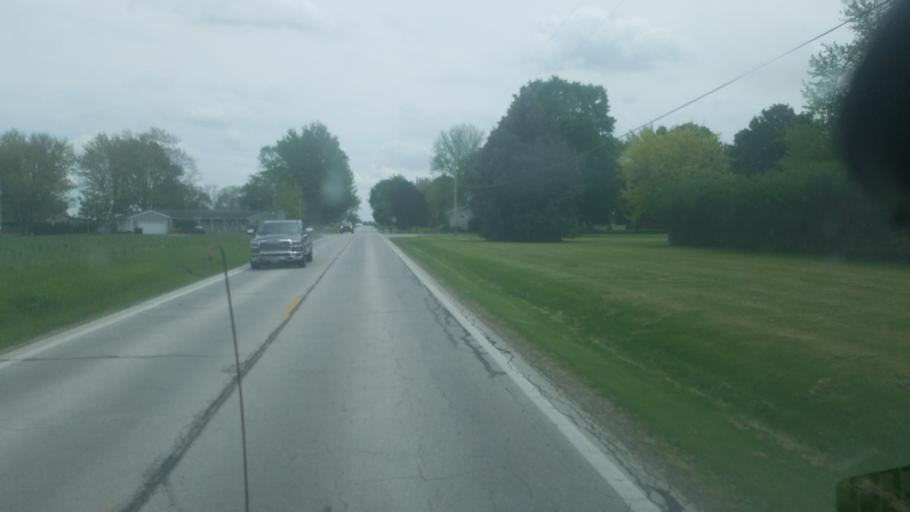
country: US
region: Ohio
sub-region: Seneca County
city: Tiffin
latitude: 41.0665
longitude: -83.1436
